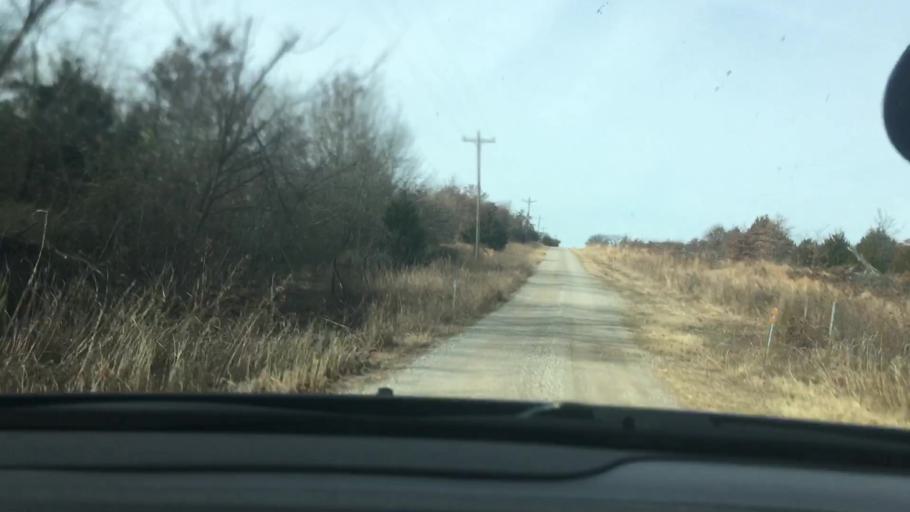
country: US
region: Oklahoma
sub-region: Garvin County
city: Wynnewood
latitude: 34.6374
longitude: -97.2365
